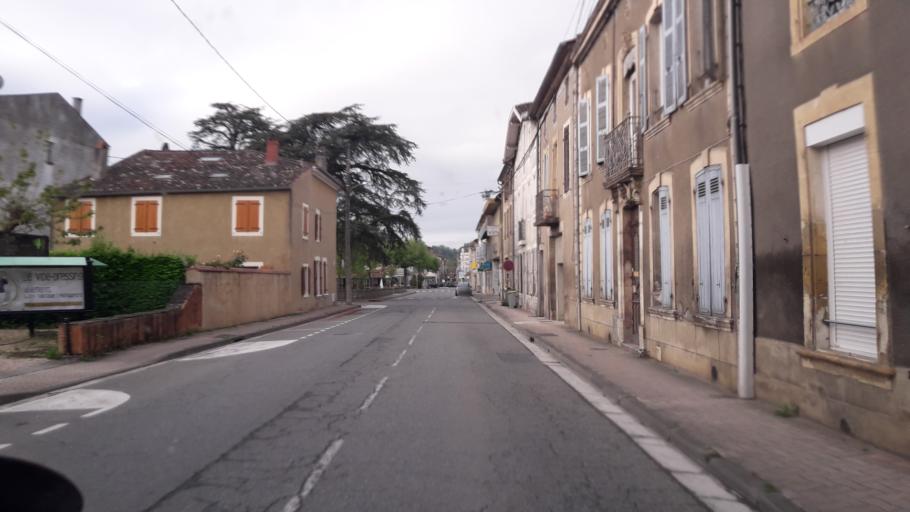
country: FR
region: Midi-Pyrenees
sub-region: Departement de la Haute-Garonne
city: Cazeres
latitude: 43.2092
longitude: 1.0857
